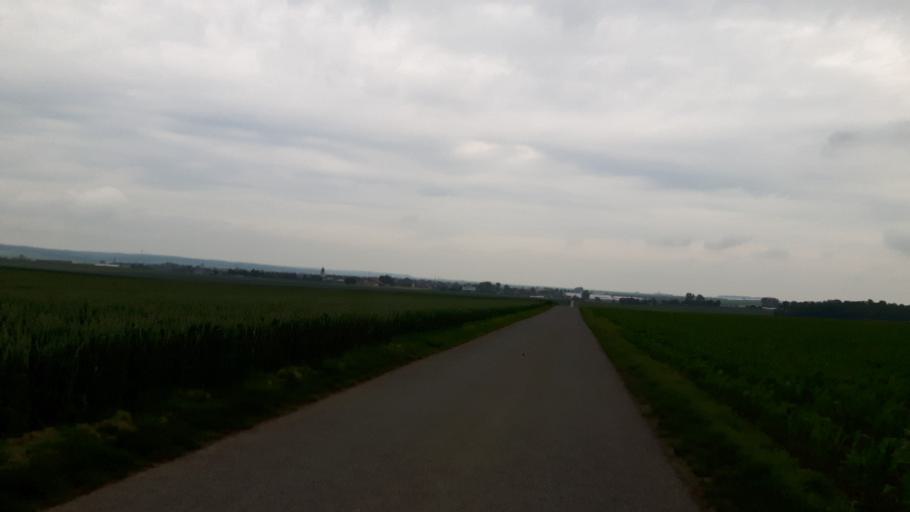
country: DE
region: Bavaria
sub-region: Regierungsbezirk Unterfranken
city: Unterpleichfeld
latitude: 49.8553
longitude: 10.0569
